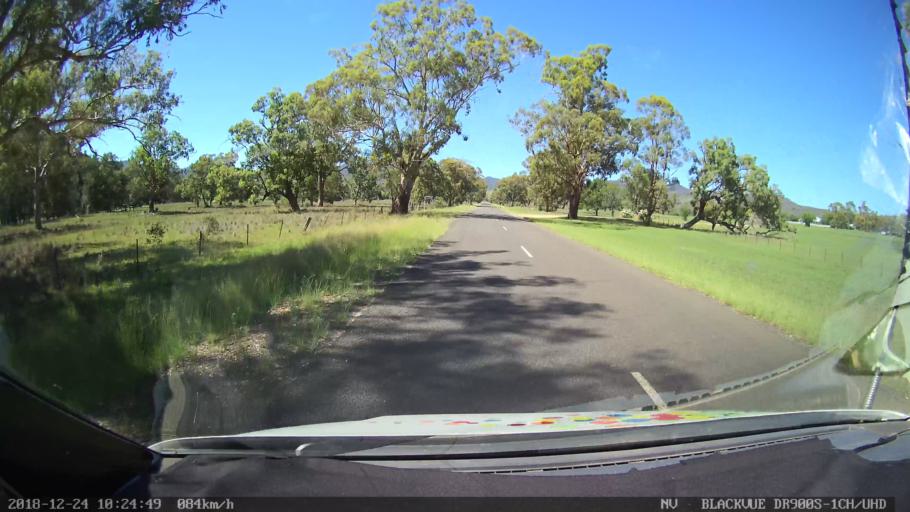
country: AU
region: New South Wales
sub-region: Liverpool Plains
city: Quirindi
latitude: -31.7911
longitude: 150.5312
